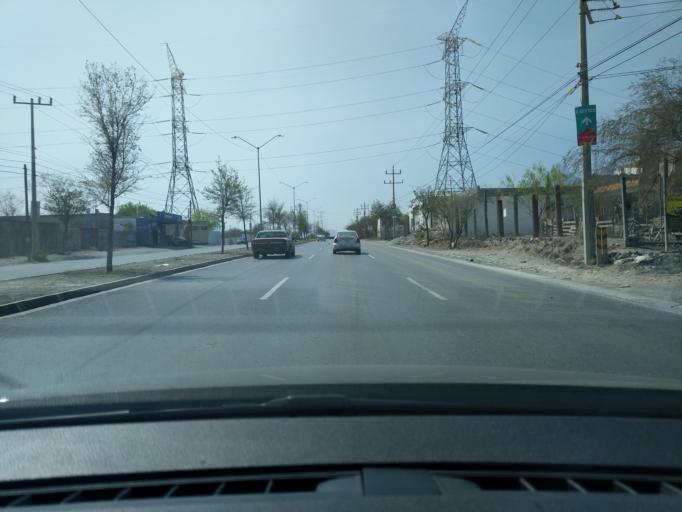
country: MX
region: Nuevo Leon
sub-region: Garcia
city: Valle de Lincoln
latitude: 25.7904
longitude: -100.5008
